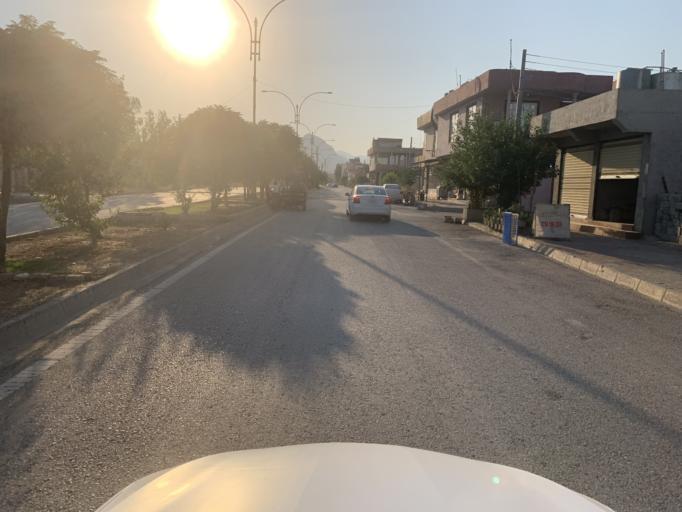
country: IQ
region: As Sulaymaniyah
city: Raniye
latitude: 36.2379
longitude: 44.8808
